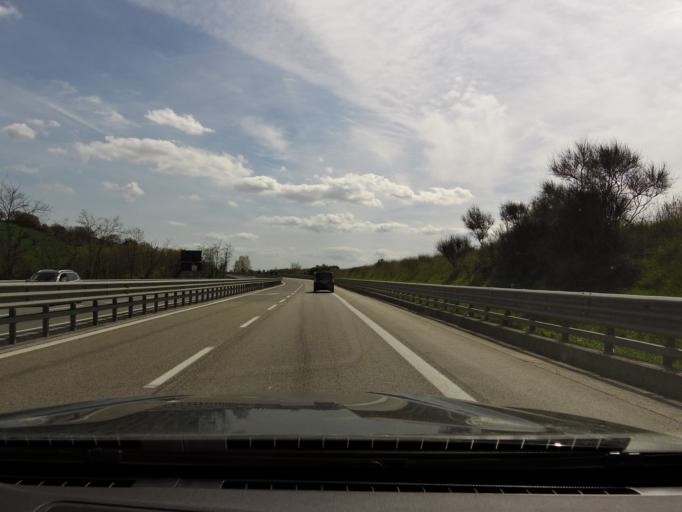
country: IT
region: The Marches
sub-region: Provincia di Ancona
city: San Biagio
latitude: 43.5392
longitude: 13.5153
